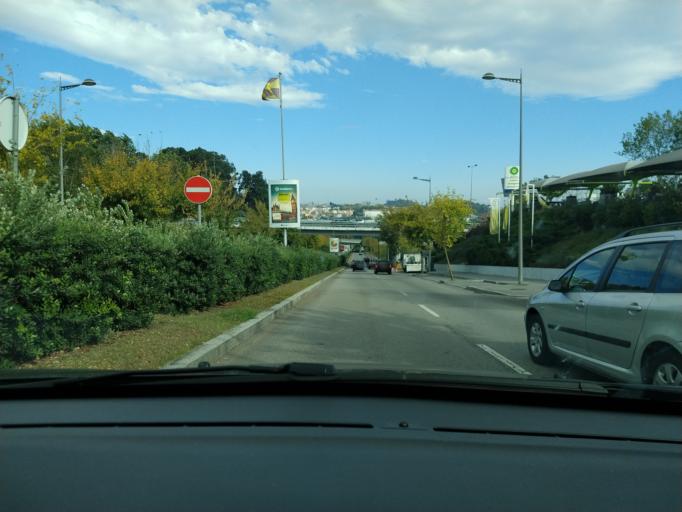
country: PT
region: Porto
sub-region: Vila Nova de Gaia
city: Oliveira do Douro
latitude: 41.1267
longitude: -8.5982
